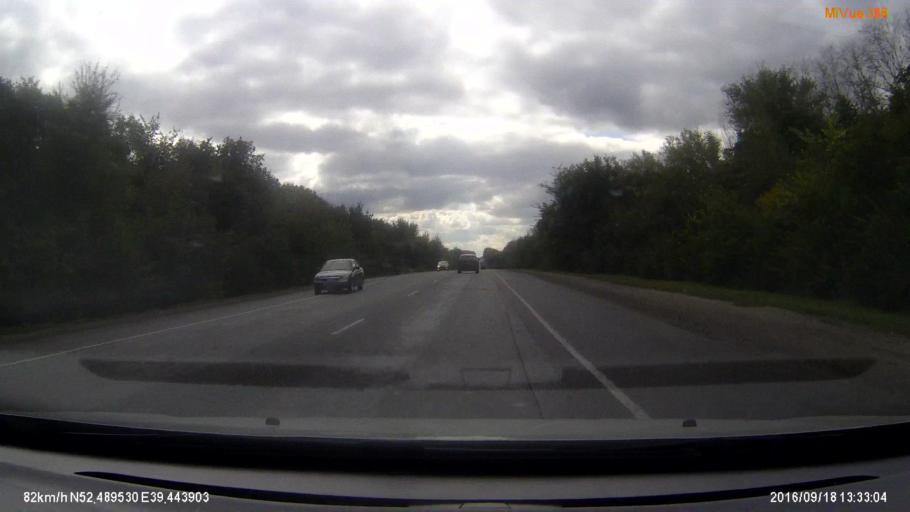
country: RU
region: Lipetsk
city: Borinskoye
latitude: 52.4572
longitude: 39.3827
